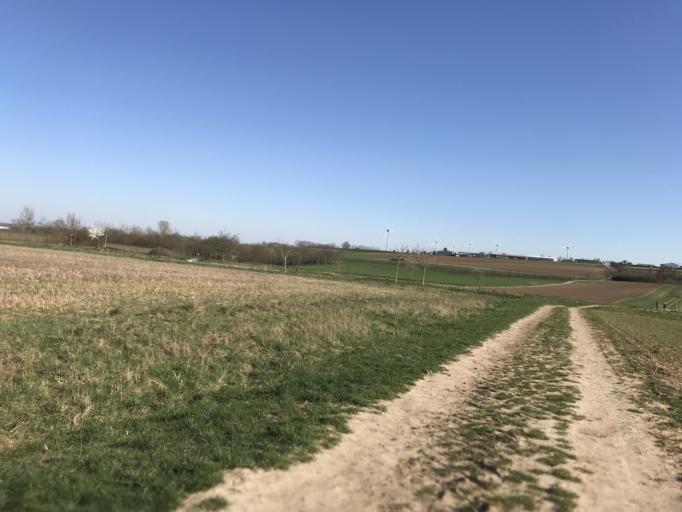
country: DE
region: Rheinland-Pfalz
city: Klein-Winternheim
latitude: 49.9585
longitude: 8.2097
